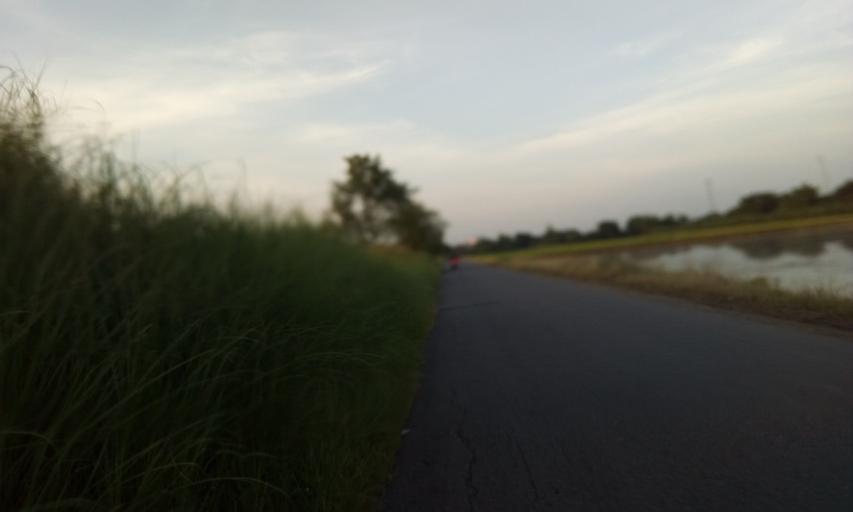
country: TH
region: Pathum Thani
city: Nong Suea
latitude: 14.0625
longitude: 100.8677
